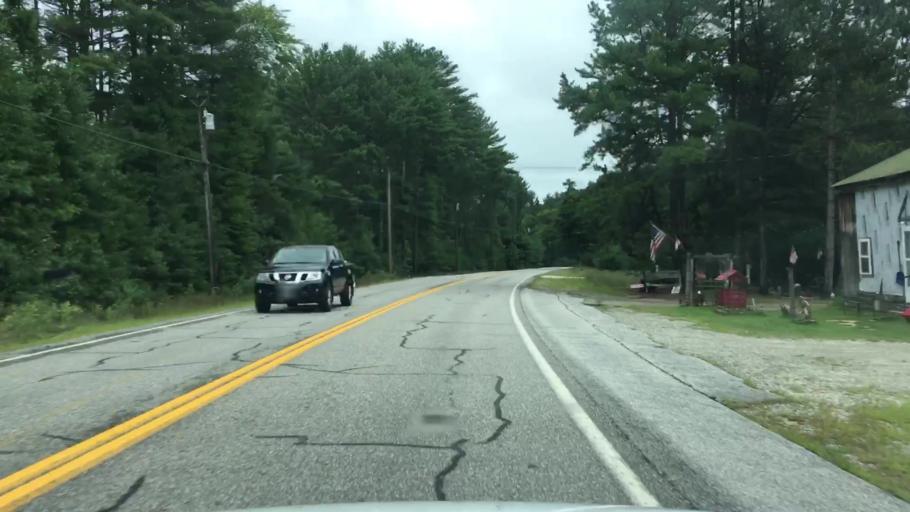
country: US
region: Maine
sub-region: Oxford County
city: Hiram
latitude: 43.8935
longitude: -70.8238
